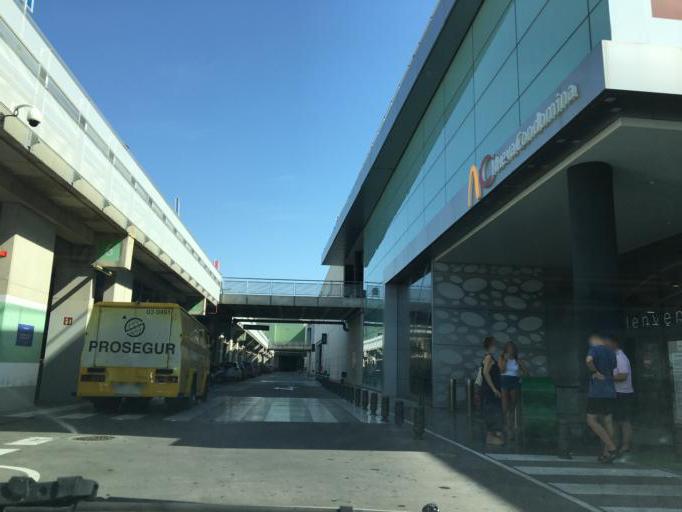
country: ES
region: Murcia
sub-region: Murcia
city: Murcia
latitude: 38.0384
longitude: -1.1494
